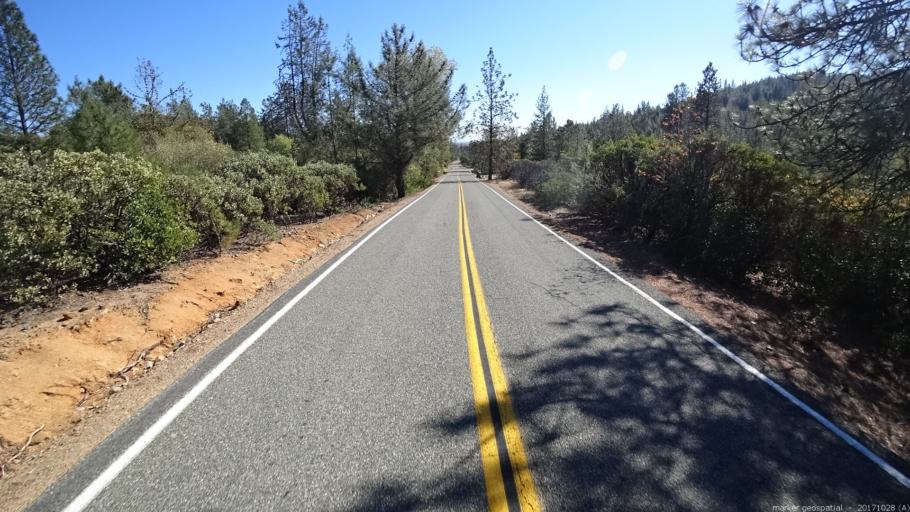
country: US
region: California
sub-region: Shasta County
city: Shasta
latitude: 40.6614
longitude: -122.4710
